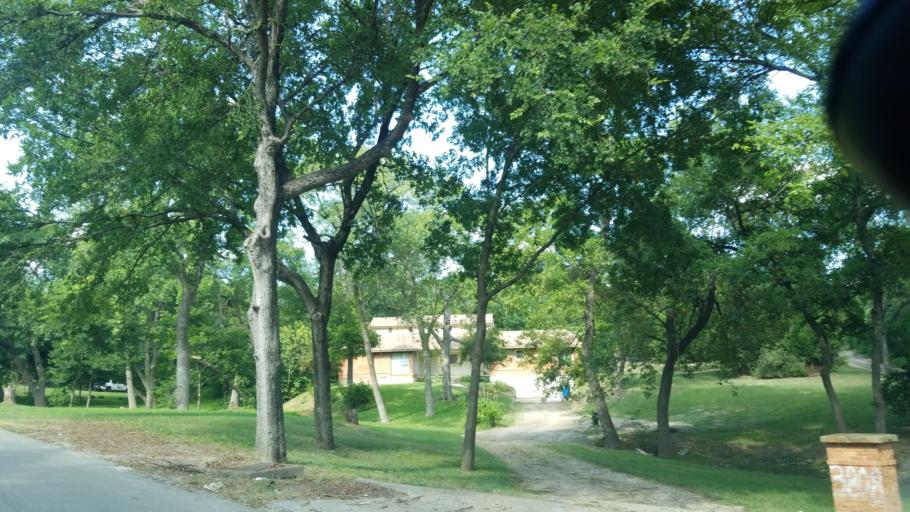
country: US
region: Texas
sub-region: Dallas County
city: Balch Springs
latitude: 32.7721
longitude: -96.7090
